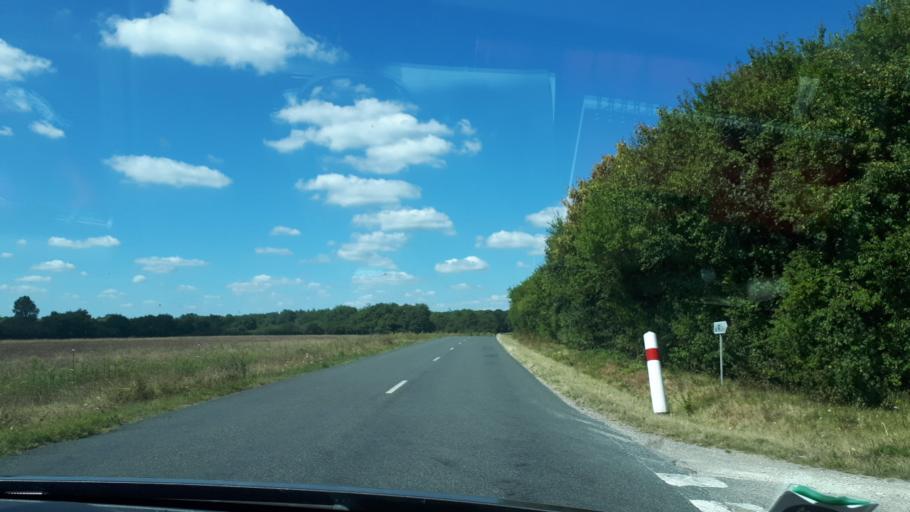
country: FR
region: Centre
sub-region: Departement du Loir-et-Cher
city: Neung-sur-Beuvron
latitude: 47.5350
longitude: 1.7855
